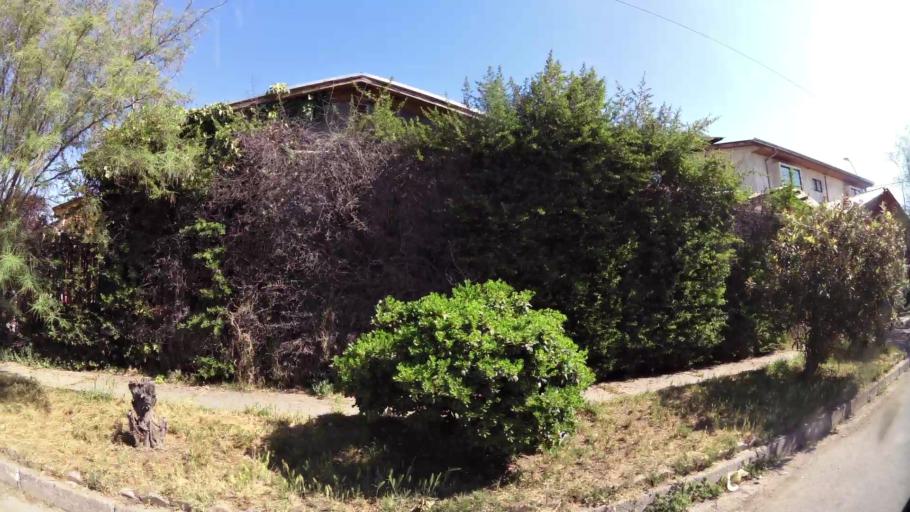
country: CL
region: Santiago Metropolitan
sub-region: Provincia de Maipo
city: San Bernardo
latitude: -33.6084
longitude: -70.7066
